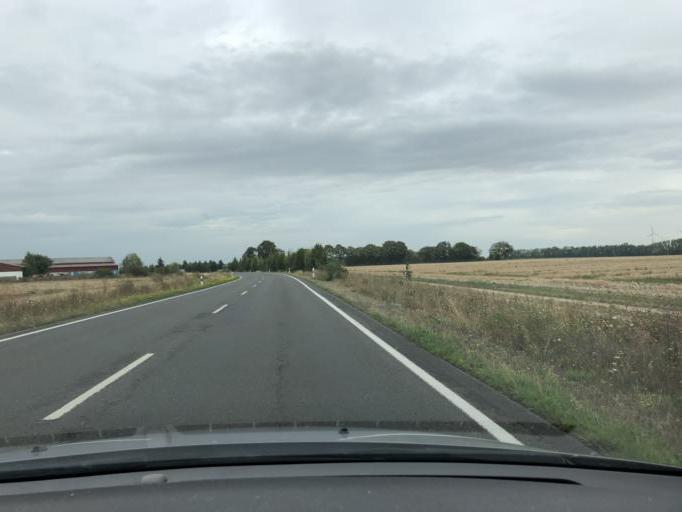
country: DE
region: Saxony-Anhalt
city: Hohendodeleben
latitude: 52.0733
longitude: 11.4814
